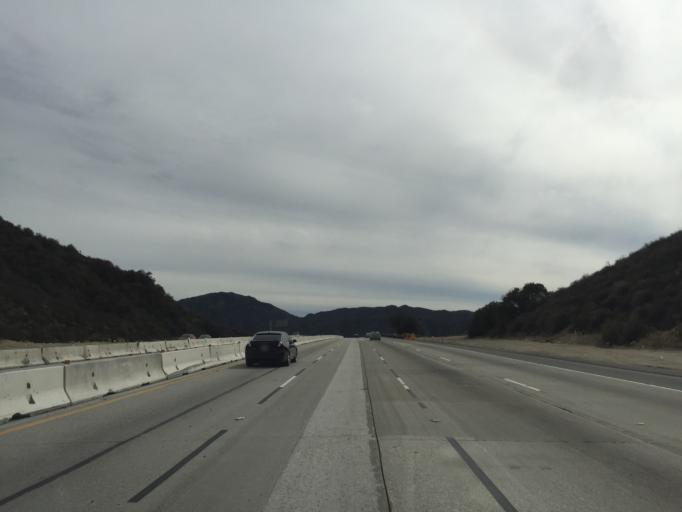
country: US
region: California
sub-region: Los Angeles County
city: Burbank
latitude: 34.2504
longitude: -118.3227
